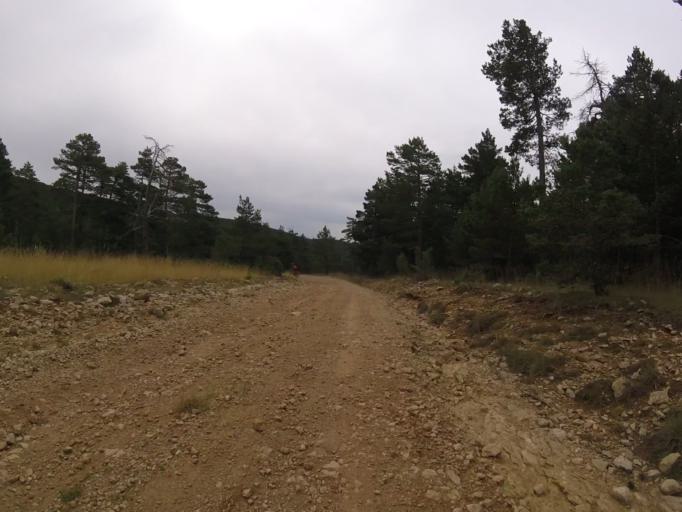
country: ES
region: Aragon
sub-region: Provincia de Teruel
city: Valdelinares
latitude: 40.3605
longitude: -0.6126
